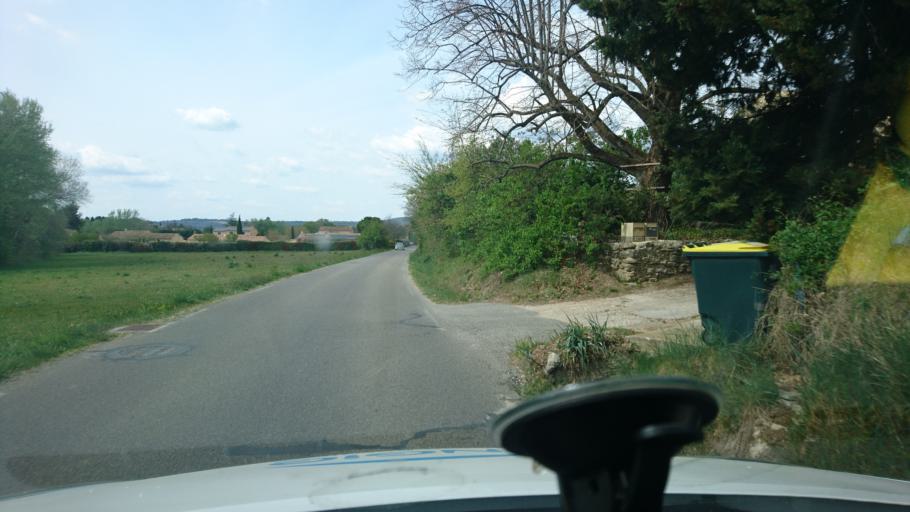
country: FR
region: Provence-Alpes-Cote d'Azur
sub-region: Departement du Vaucluse
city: Oppede
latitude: 43.8497
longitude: 5.1632
